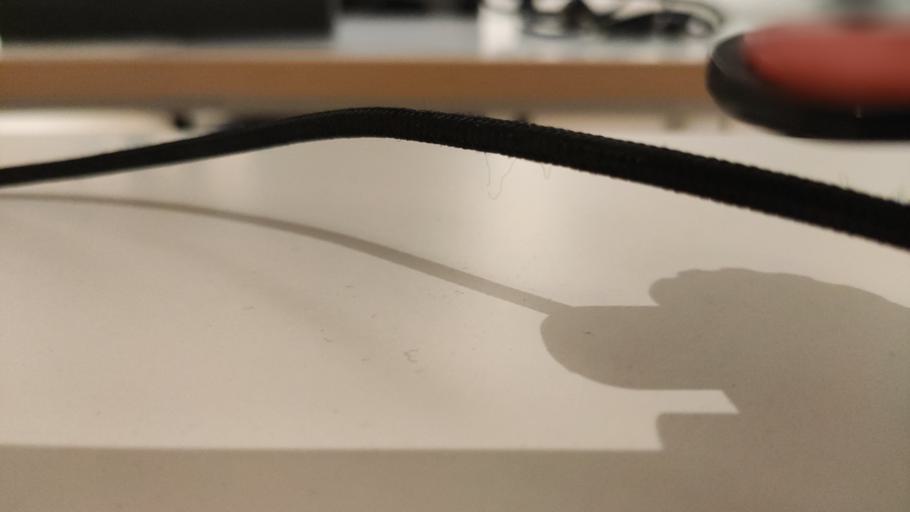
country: RU
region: Kaluga
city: Belousovo
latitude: 55.1443
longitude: 36.7661
